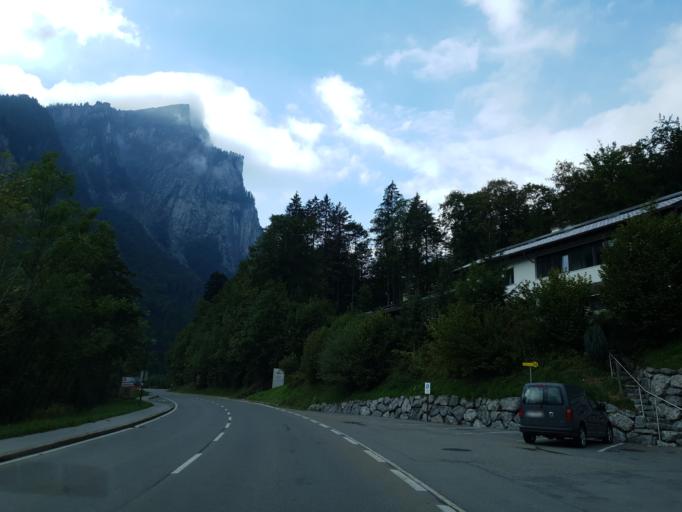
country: AT
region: Vorarlberg
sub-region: Politischer Bezirk Bregenz
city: Au
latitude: 47.3283
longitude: 9.9752
